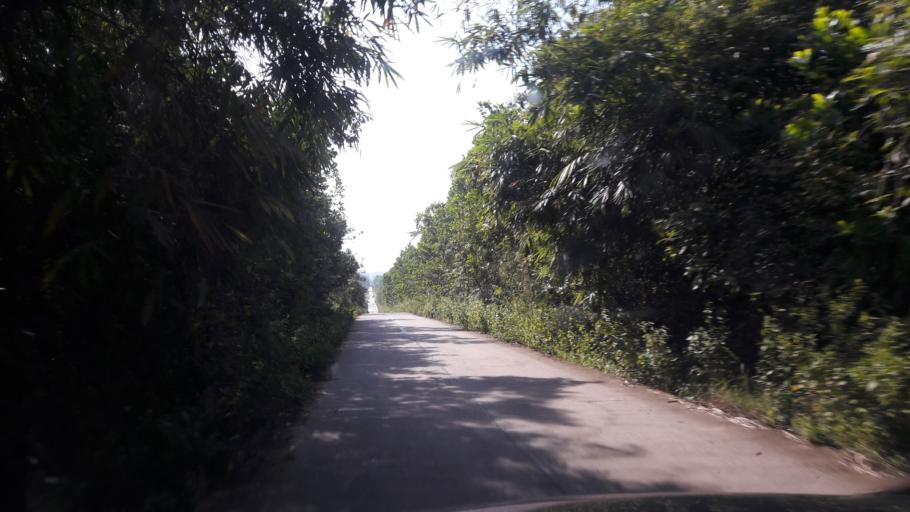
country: ID
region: South Sumatra
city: Gunungmegang Dalam
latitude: -3.3150
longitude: 103.9357
